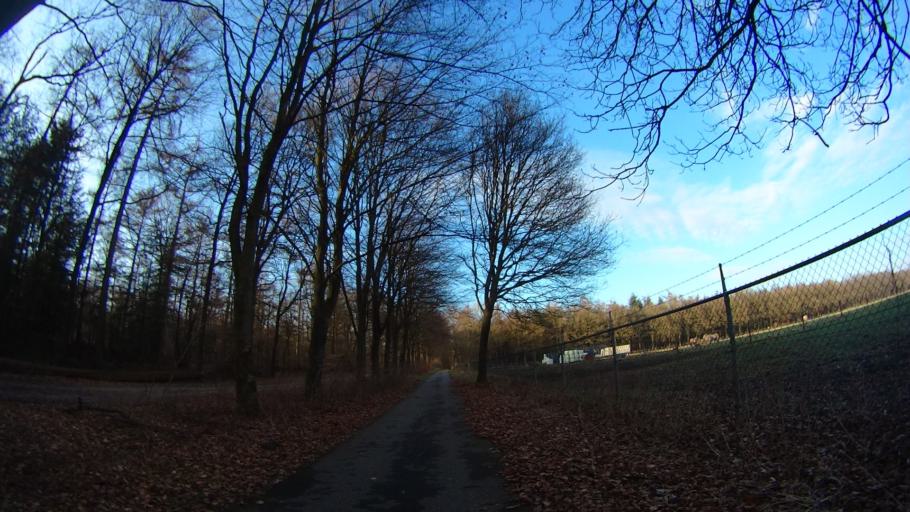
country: NL
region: Drenthe
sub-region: Gemeente Coevorden
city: Sleen
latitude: 52.8196
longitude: 6.7674
